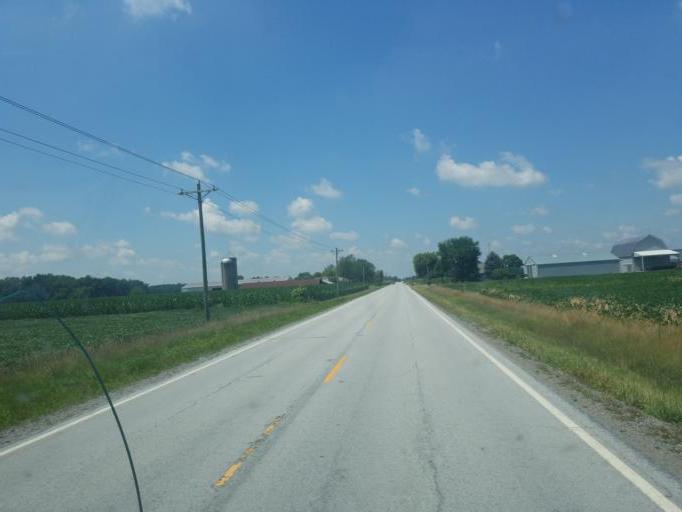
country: US
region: Ohio
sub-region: Allen County
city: Spencerville
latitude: 40.7141
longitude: -84.4058
